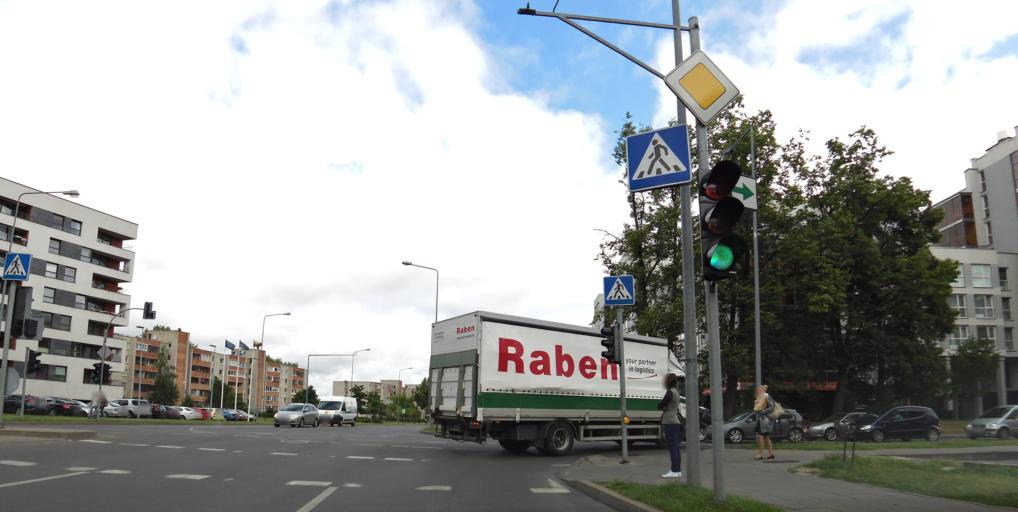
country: LT
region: Vilnius County
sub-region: Vilnius
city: Vilnius
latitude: 54.7081
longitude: 25.2909
